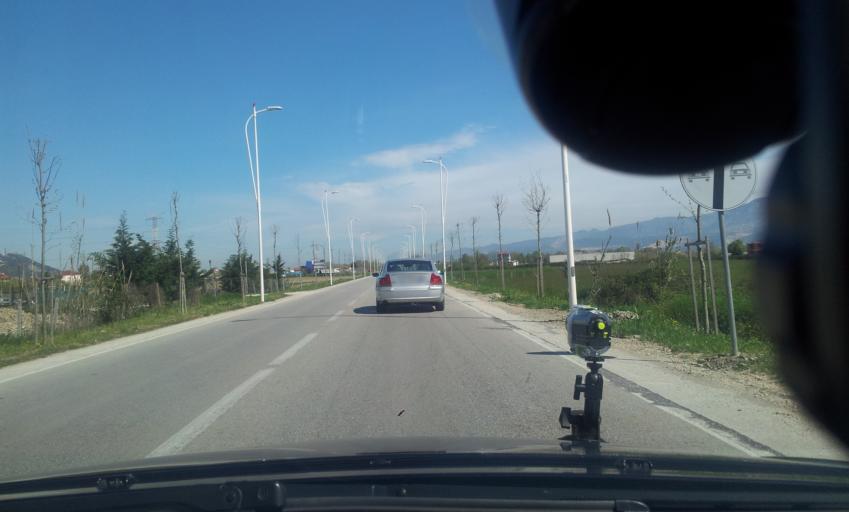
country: AL
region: Tirane
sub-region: Rrethi i Tiranes
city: Berxull
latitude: 41.3802
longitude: 19.7038
